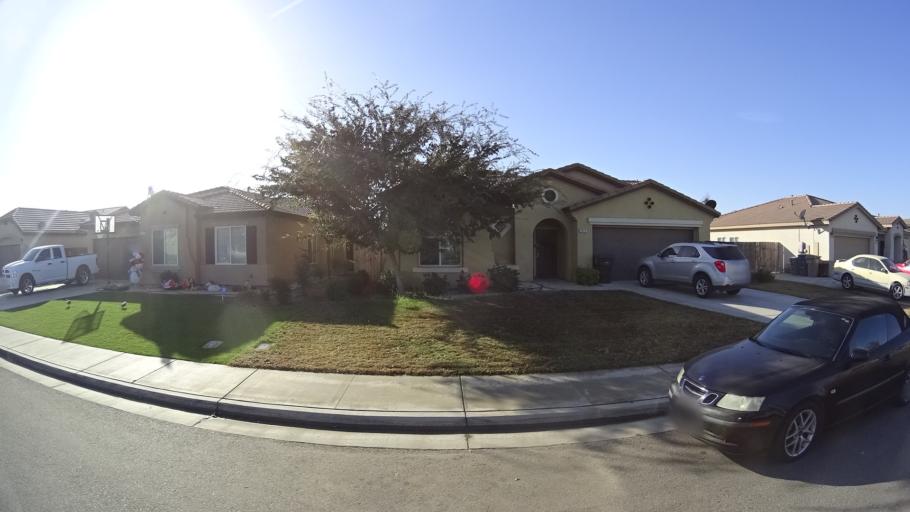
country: US
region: California
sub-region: Kern County
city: Greenfield
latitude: 35.2736
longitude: -119.0284
